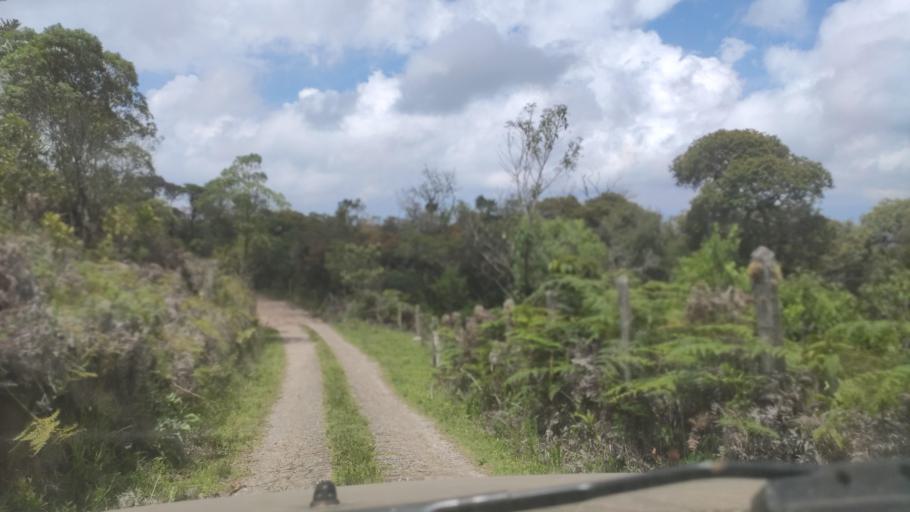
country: BR
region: Minas Gerais
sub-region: Cambui
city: Cambui
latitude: -22.6921
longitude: -45.9588
